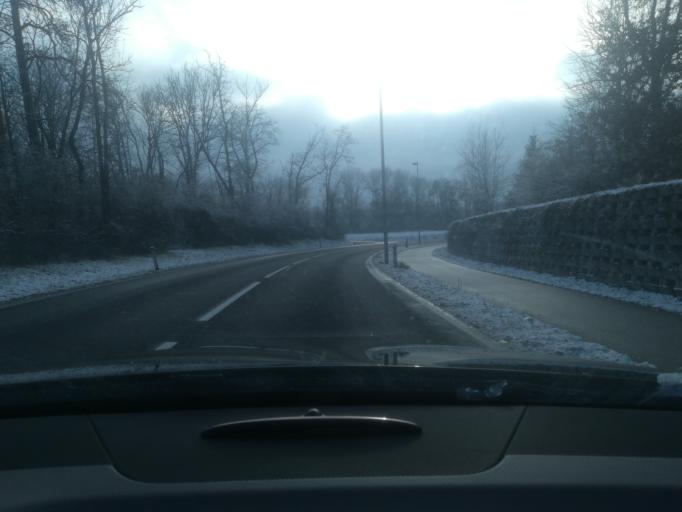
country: AT
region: Upper Austria
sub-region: Wels-Land
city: Marchtrenk
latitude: 48.1798
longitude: 14.1212
